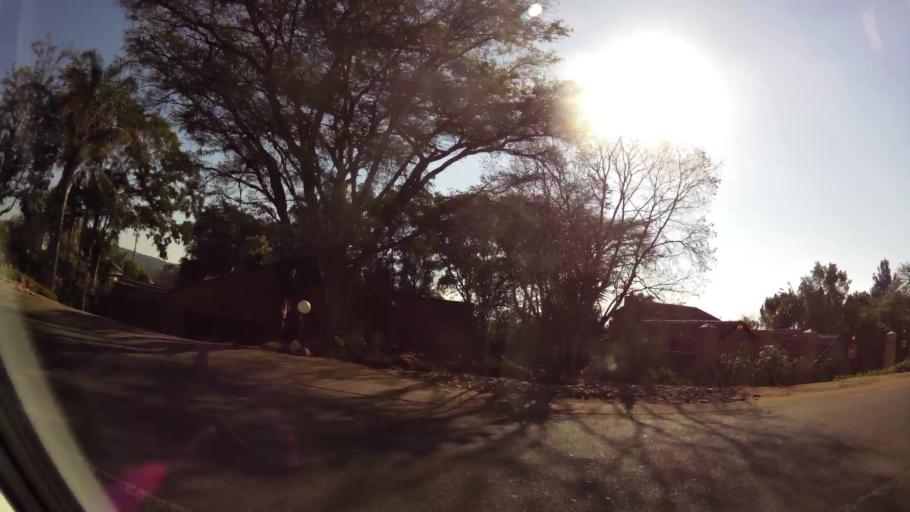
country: ZA
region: Gauteng
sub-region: City of Tshwane Metropolitan Municipality
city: Pretoria
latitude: -25.7950
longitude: 28.3063
